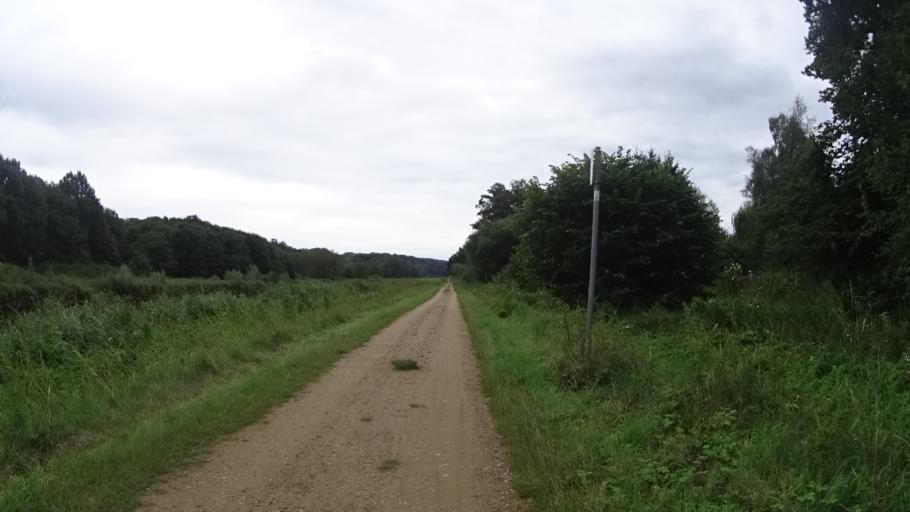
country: DE
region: Schleswig-Holstein
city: Alt Molln
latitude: 53.6435
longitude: 10.6517
